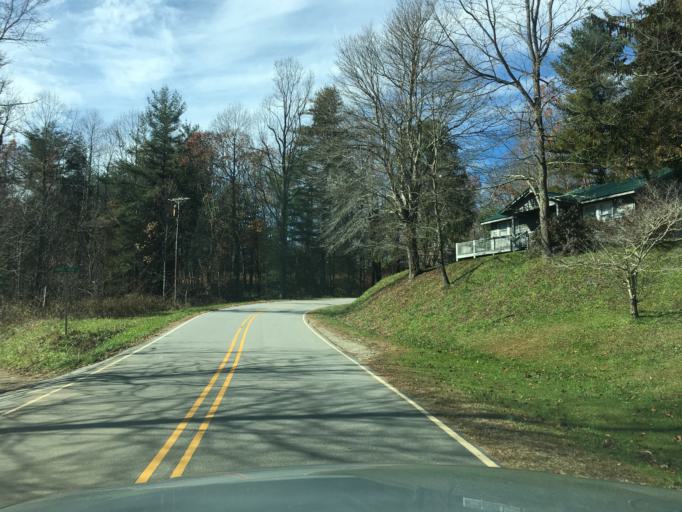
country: US
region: North Carolina
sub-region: Henderson County
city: Valley Hill
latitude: 35.2321
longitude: -82.5098
